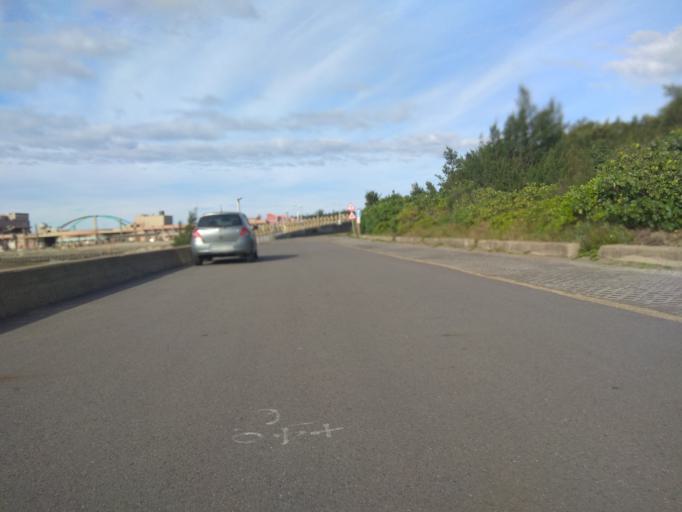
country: TW
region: Taiwan
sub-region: Hsinchu
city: Zhubei
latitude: 24.9853
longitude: 121.0162
